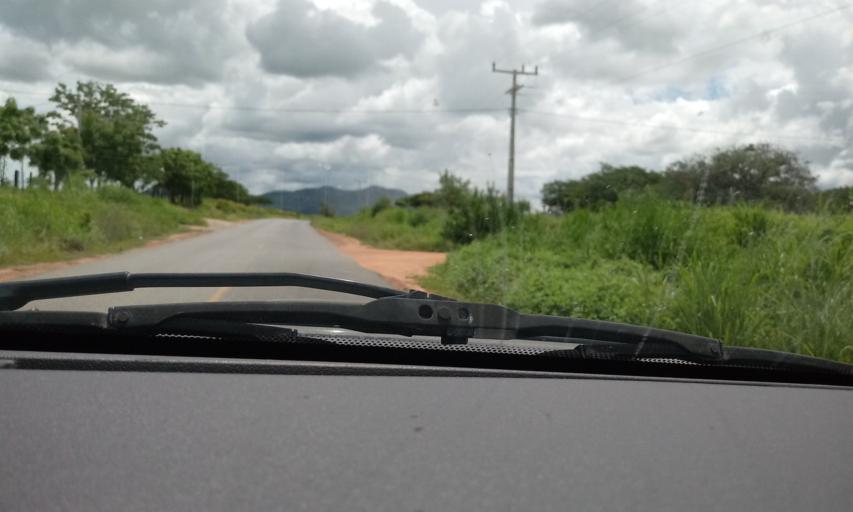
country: BR
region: Bahia
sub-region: Guanambi
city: Guanambi
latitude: -14.1754
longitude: -42.8014
